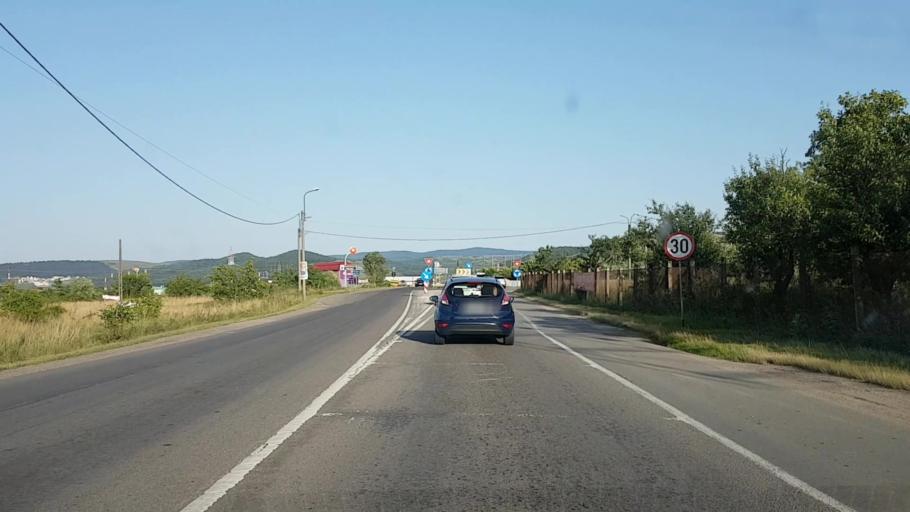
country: RO
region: Cluj
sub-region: Comuna Floresti
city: Luna de Sus
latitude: 46.7460
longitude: 23.4506
